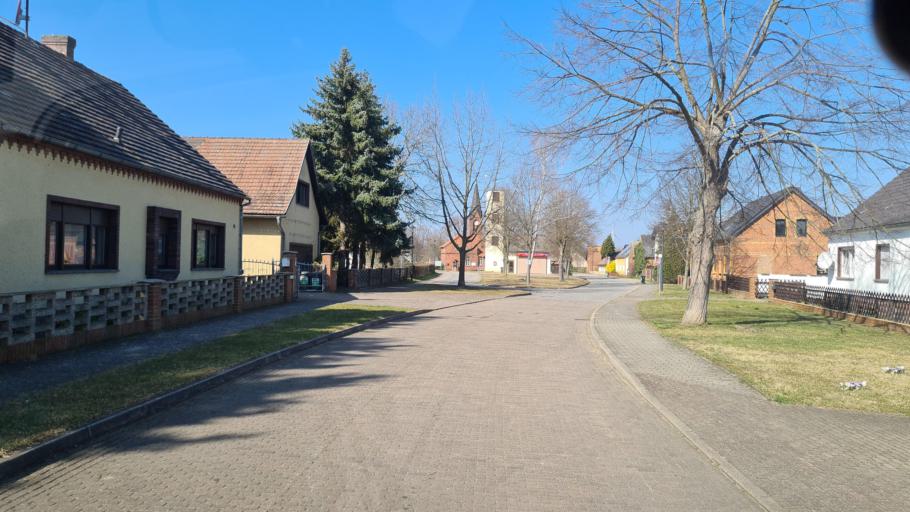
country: DE
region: Brandenburg
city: Calau
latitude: 51.7986
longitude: 13.9744
